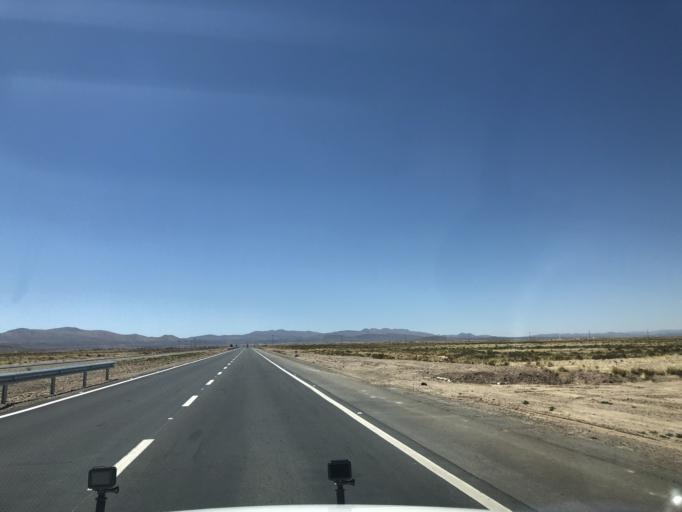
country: BO
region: La Paz
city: Colquiri
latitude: -17.6503
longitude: -67.1870
